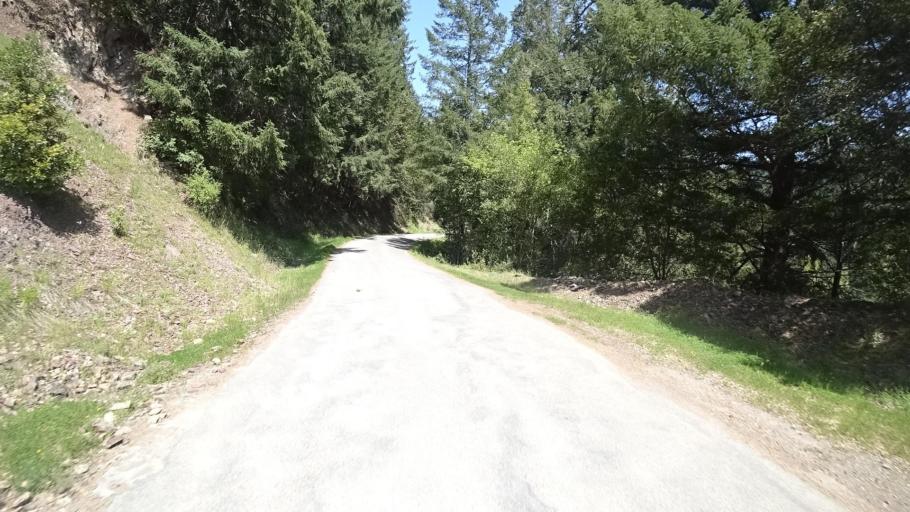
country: US
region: California
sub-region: Humboldt County
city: Redway
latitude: 40.1960
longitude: -123.5261
